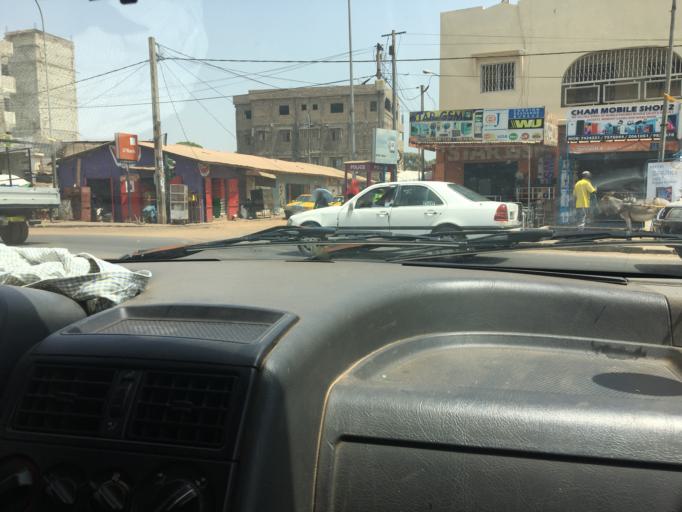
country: GM
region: Western
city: Abuko
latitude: 13.4065
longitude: -16.6657
